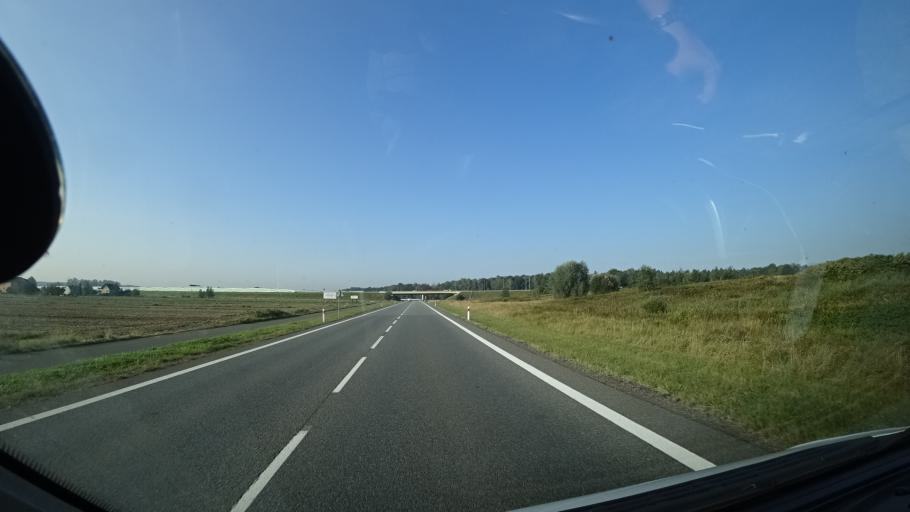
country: PL
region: Silesian Voivodeship
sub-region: Powiat gliwicki
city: Sosnicowice
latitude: 50.2805
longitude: 18.5762
